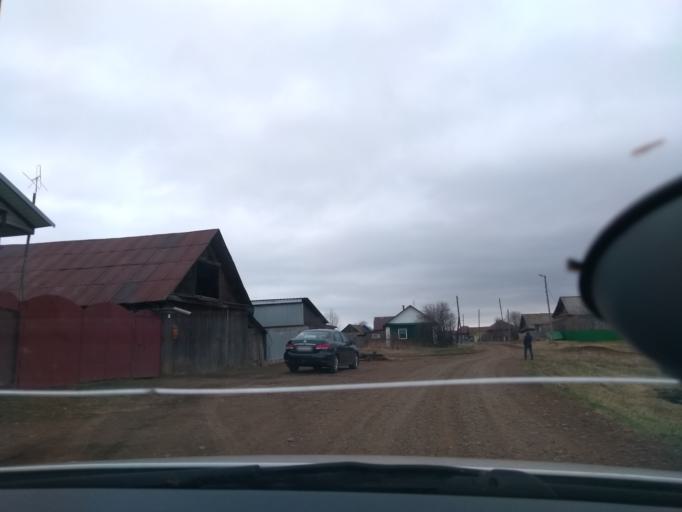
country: RU
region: Perm
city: Orda
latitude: 57.2196
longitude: 56.5915
